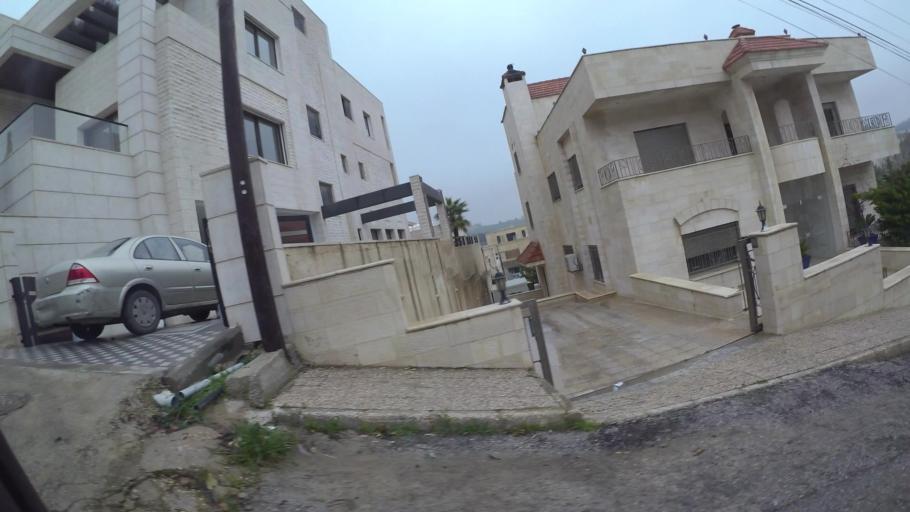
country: JO
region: Amman
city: Al Jubayhah
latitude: 32.0031
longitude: 35.8207
